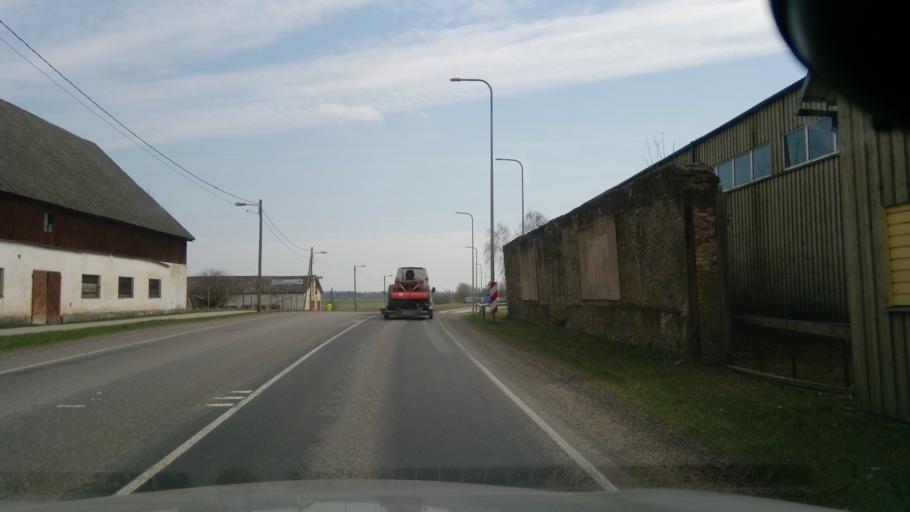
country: EE
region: Jaervamaa
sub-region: Tueri vald
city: Sarevere
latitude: 58.7847
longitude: 25.4314
